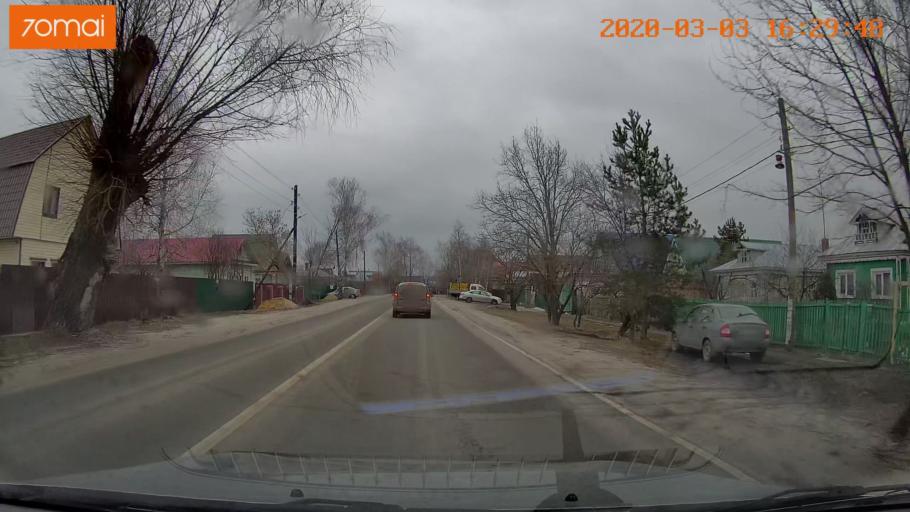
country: RU
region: Moskovskaya
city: Konobeyevo
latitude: 55.4358
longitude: 38.7048
